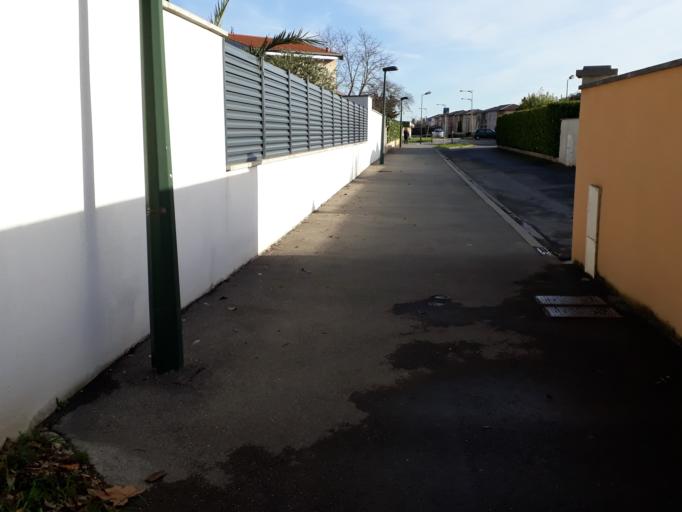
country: FR
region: Midi-Pyrenees
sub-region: Departement de la Haute-Garonne
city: Beauzelle
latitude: 43.6612
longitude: 1.3781
